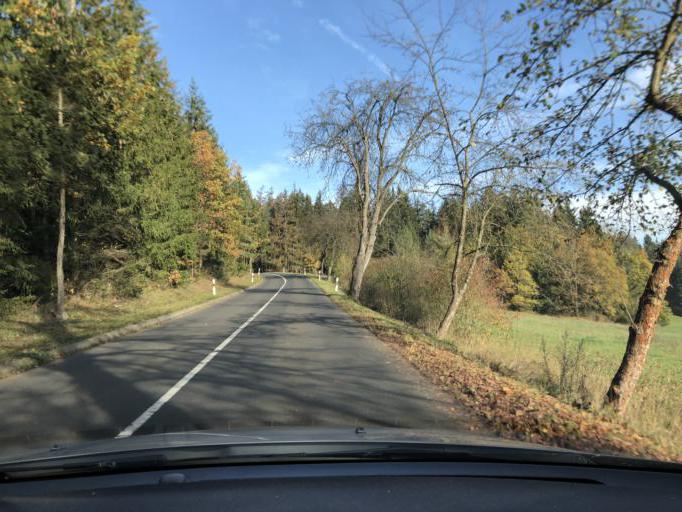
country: DE
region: Thuringia
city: Reurieth
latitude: 50.4322
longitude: 10.6361
